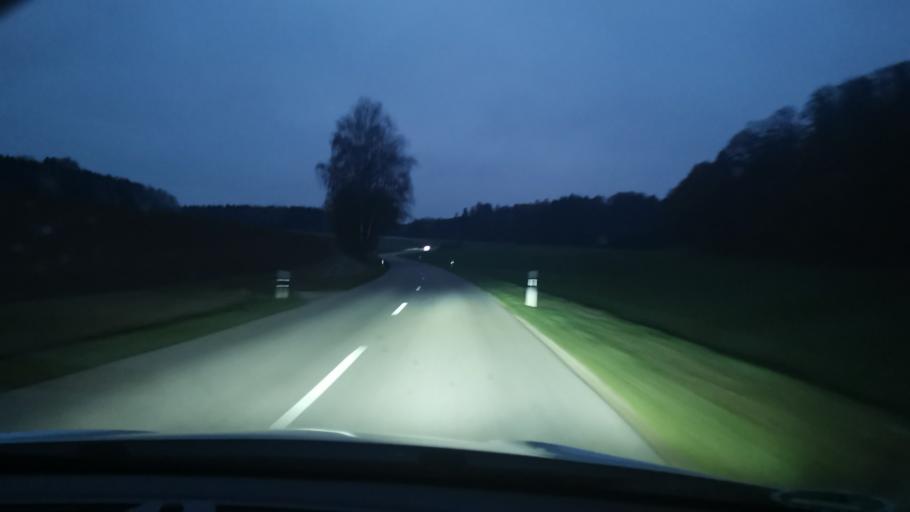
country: DE
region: Bavaria
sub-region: Swabia
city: Pottmes
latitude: 48.5675
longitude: 11.0676
